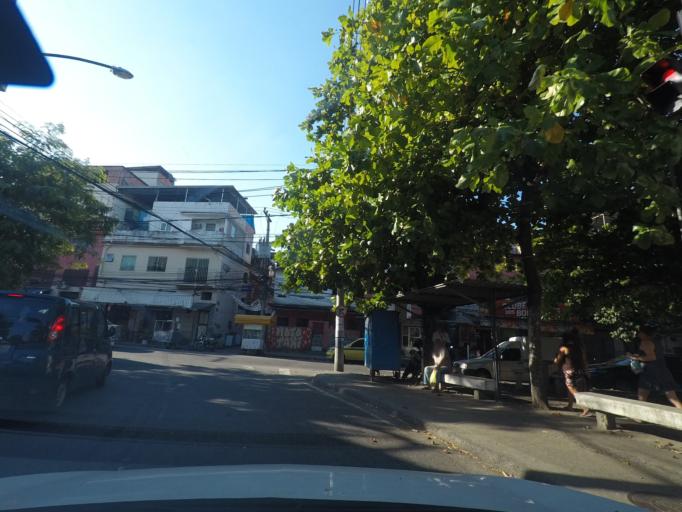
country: BR
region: Rio de Janeiro
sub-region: Rio De Janeiro
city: Rio de Janeiro
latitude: -22.8893
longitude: -43.2278
